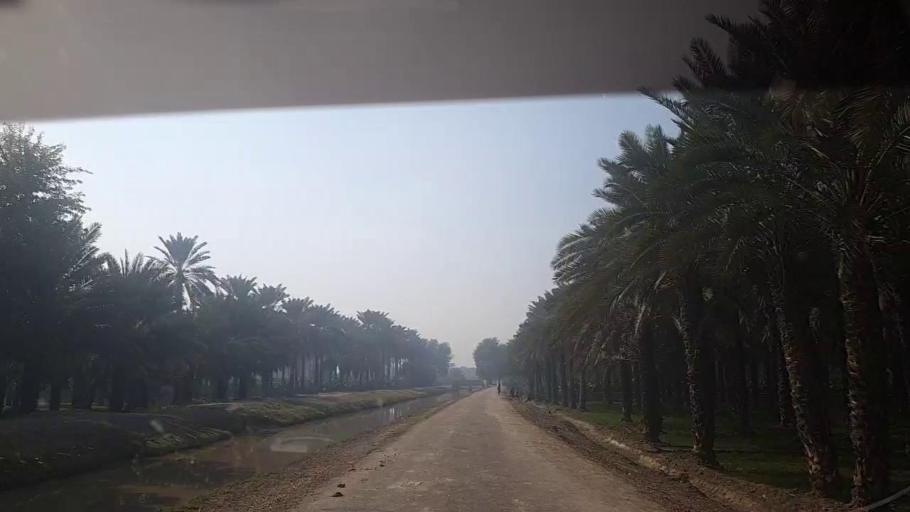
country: PK
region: Sindh
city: Khairpur
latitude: 27.4632
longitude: 68.7092
